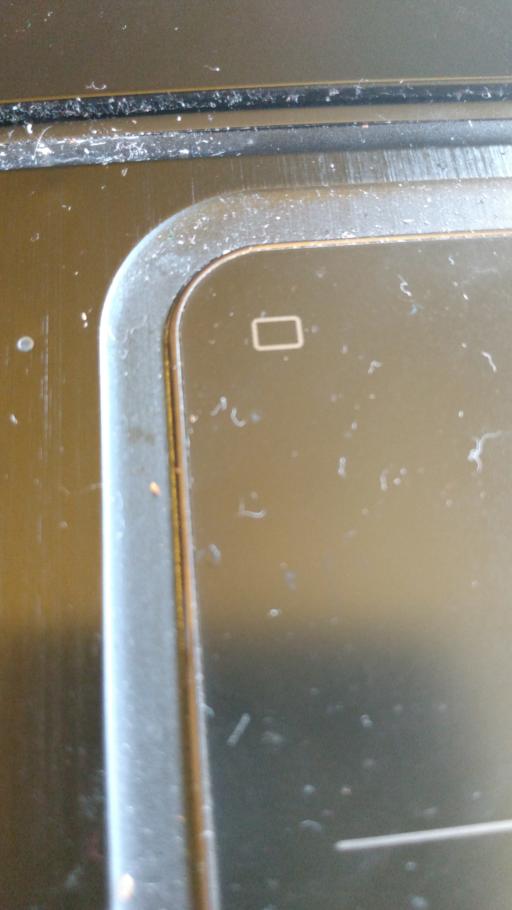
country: RU
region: Moskovskaya
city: Kolomna
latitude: 55.0488
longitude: 38.9024
